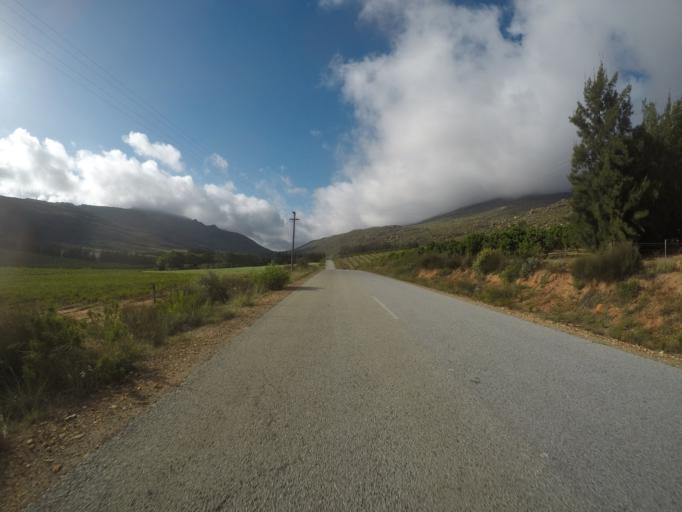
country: ZA
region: Western Cape
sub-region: West Coast District Municipality
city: Clanwilliam
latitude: -32.3560
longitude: 18.8513
